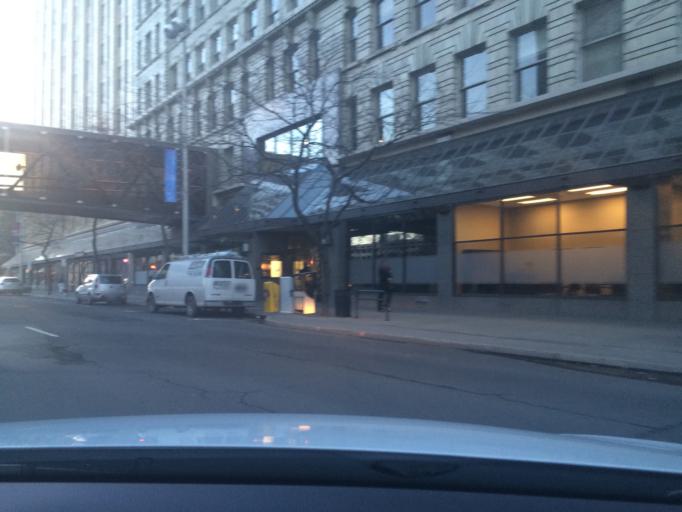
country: US
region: Washington
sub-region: Spokane County
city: Spokane
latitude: 47.6580
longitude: -117.4195
